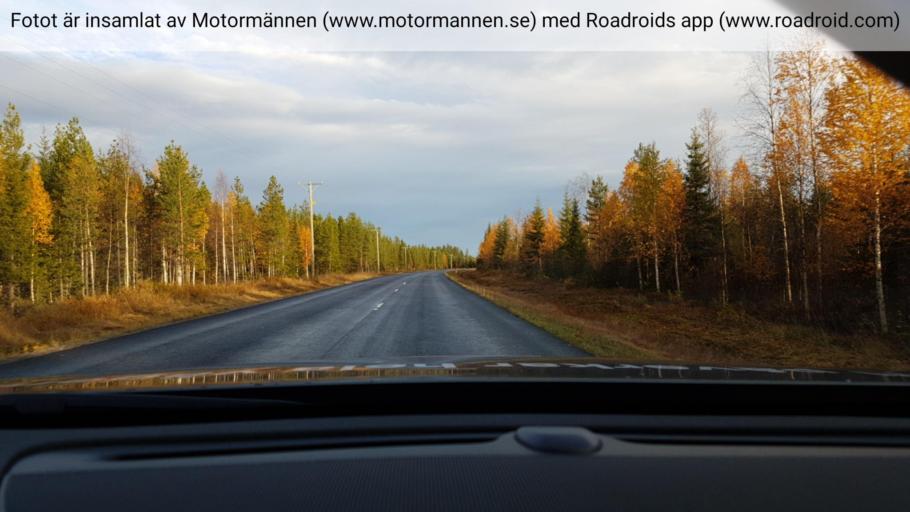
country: SE
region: Norrbotten
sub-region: Overkalix Kommun
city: OEverkalix
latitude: 66.9650
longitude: 22.6746
